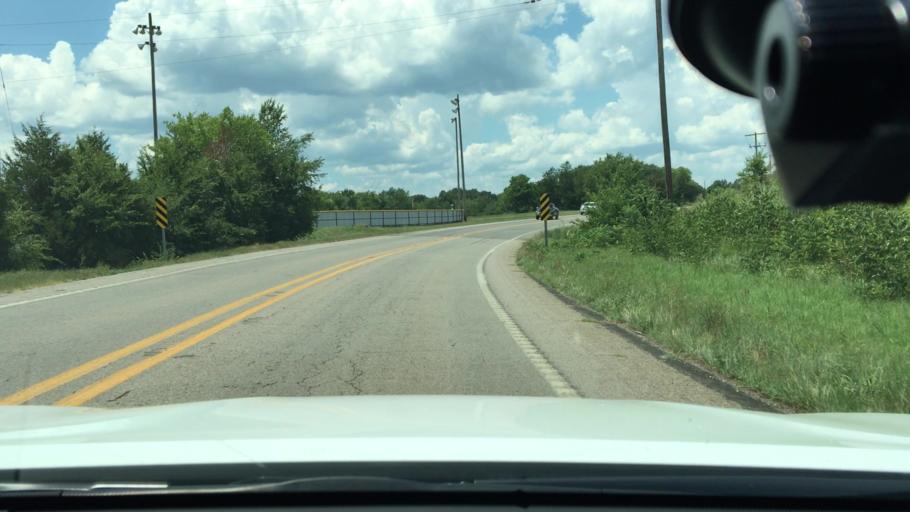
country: US
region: Arkansas
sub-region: Logan County
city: Booneville
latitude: 35.1483
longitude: -93.8343
